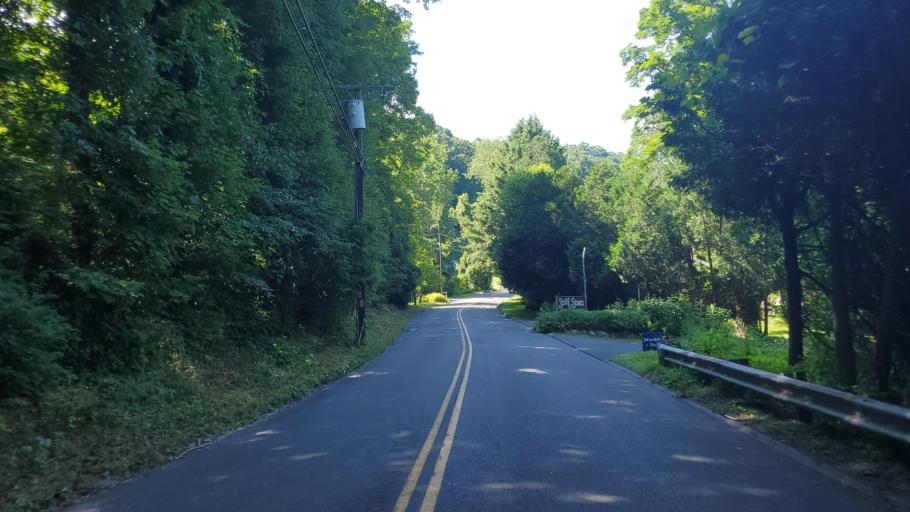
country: US
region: Connecticut
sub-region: Fairfield County
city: Newtown
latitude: 41.3405
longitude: -73.2930
